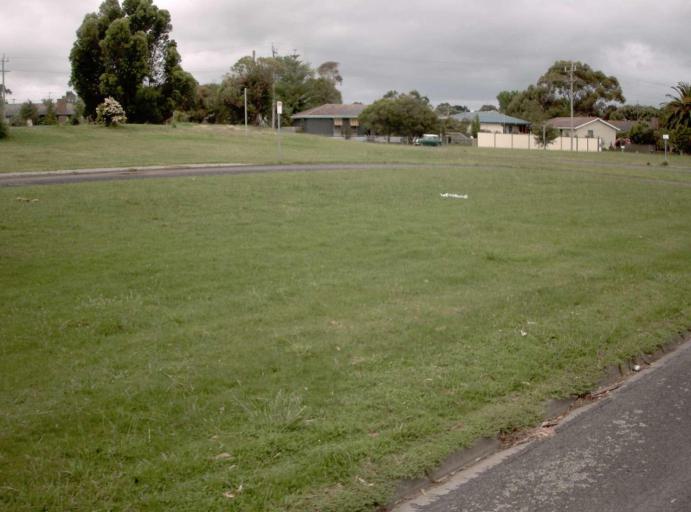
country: AU
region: Victoria
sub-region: Bass Coast
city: North Wonthaggi
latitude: -38.6010
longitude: 145.6016
